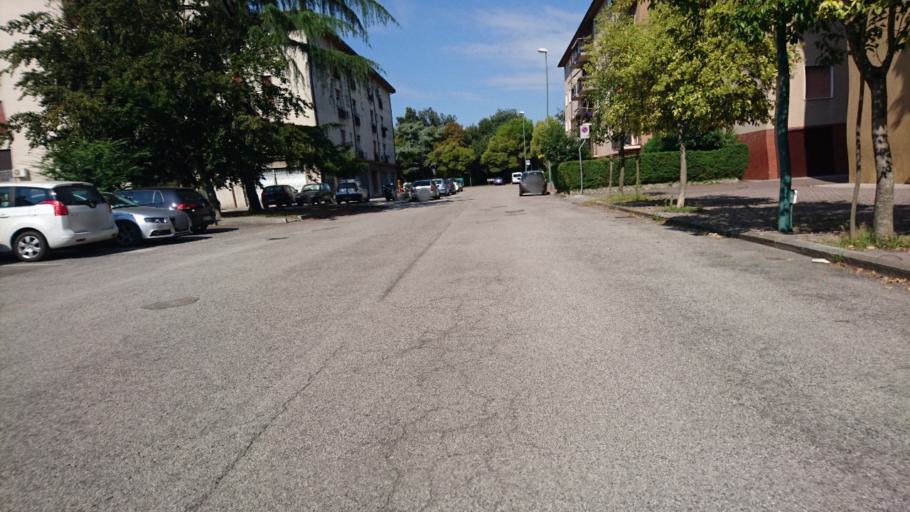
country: IT
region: Veneto
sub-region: Provincia di Venezia
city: Campalto
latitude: 45.5062
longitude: 12.2651
